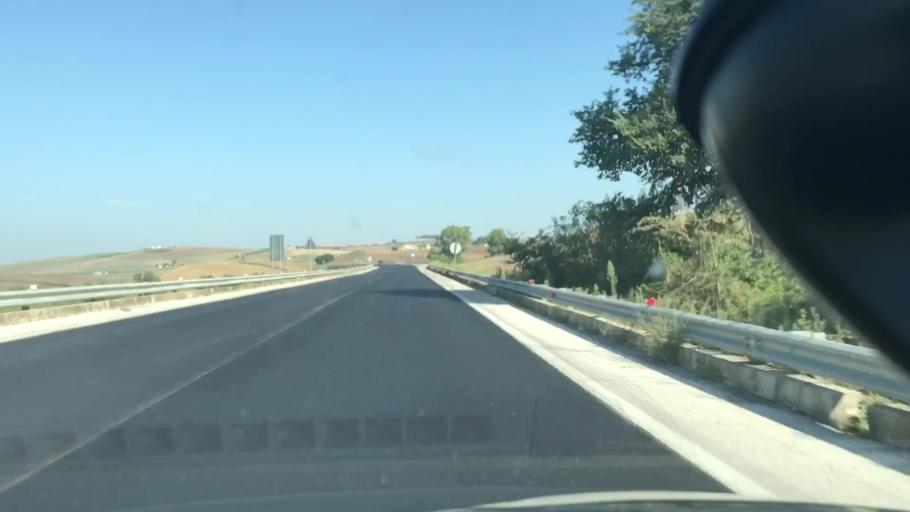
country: IT
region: Apulia
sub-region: Provincia di Barletta - Andria - Trani
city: Spinazzola
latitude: 40.9102
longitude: 16.1068
